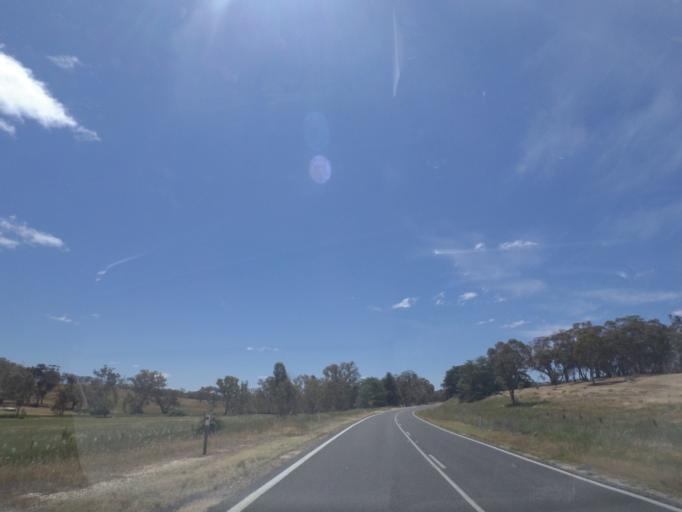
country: AU
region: Victoria
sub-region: Mount Alexander
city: Castlemaine
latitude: -37.1721
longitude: 144.1461
